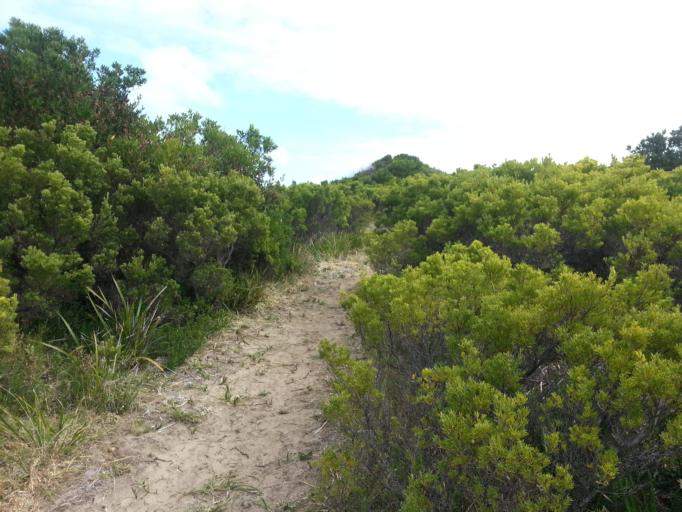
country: AU
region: Victoria
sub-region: Colac-Otway
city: Apollo Bay
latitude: -38.8548
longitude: 143.5231
